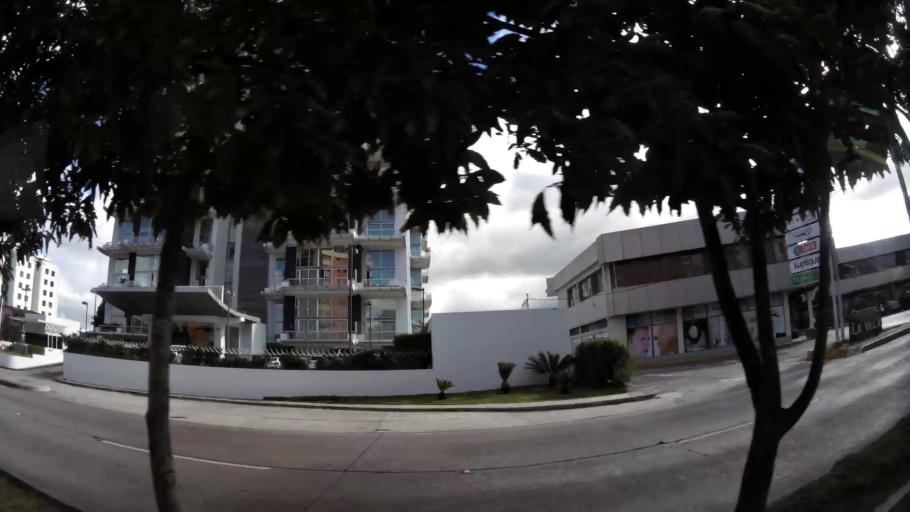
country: GT
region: Guatemala
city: Santa Catarina Pinula
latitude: 14.5911
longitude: -90.5038
